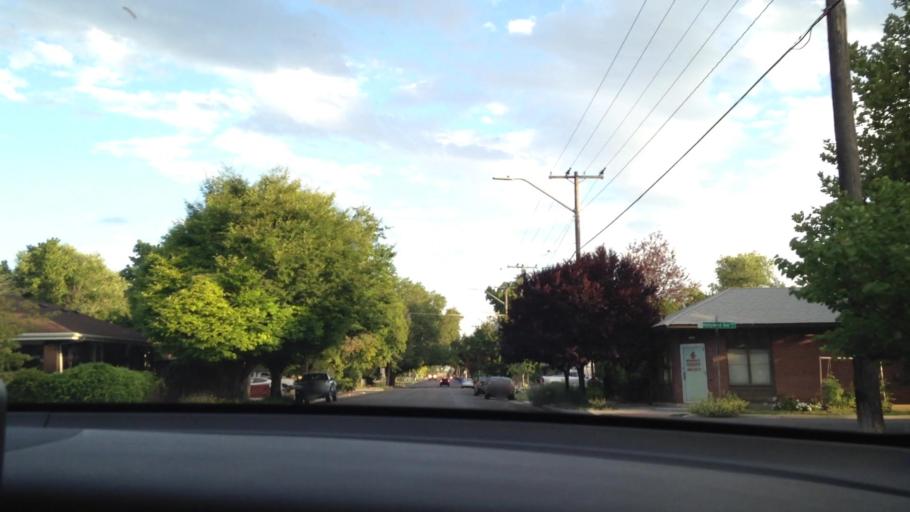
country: US
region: Utah
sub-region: Salt Lake County
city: South Salt Lake
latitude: 40.7274
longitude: -111.8797
